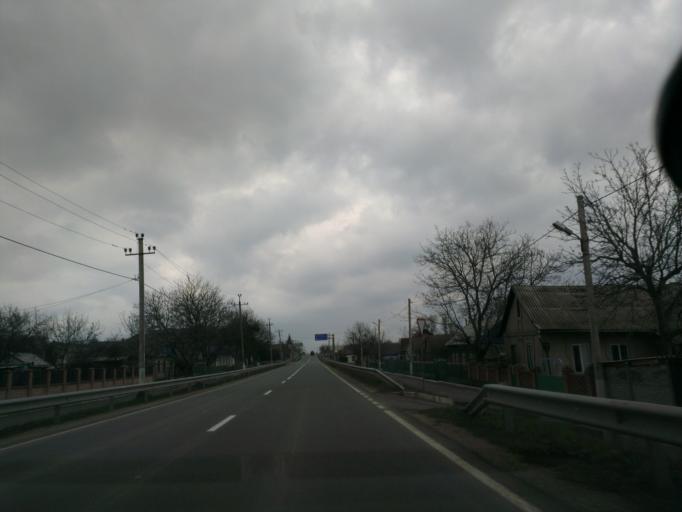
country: MD
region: Cimislia
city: Cimislia
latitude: 46.6217
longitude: 28.7249
